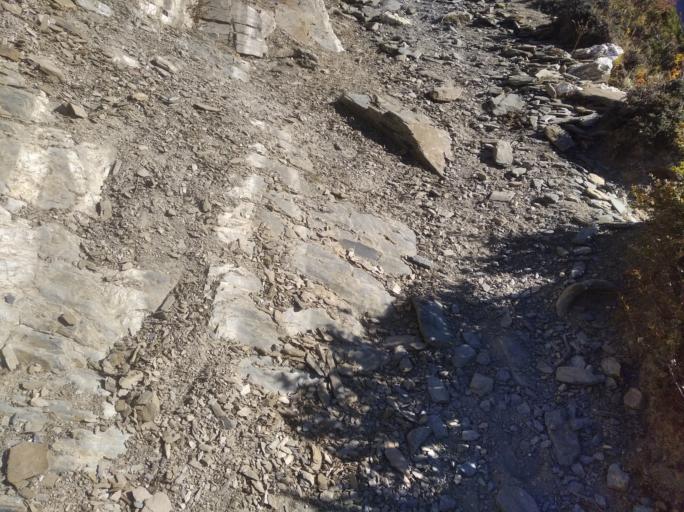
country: NP
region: Western Region
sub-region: Dhawalagiri Zone
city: Jomsom
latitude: 28.9070
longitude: 83.3717
